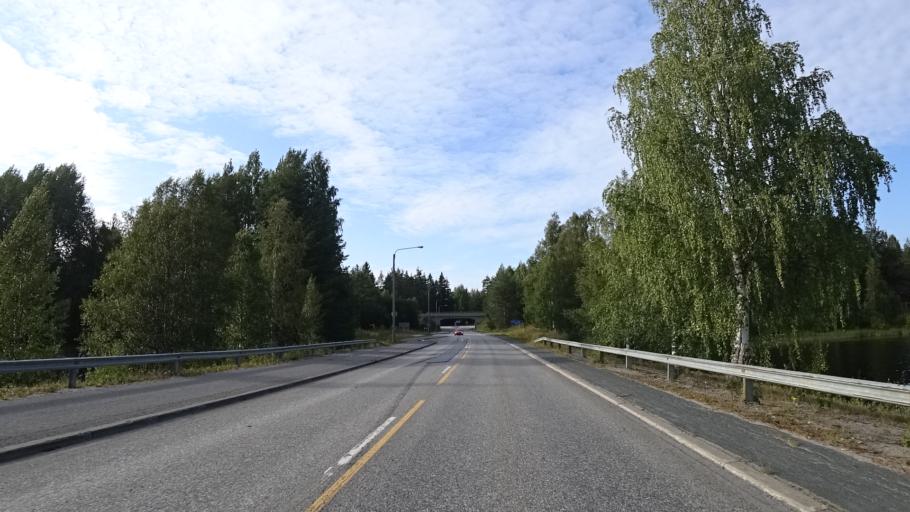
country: FI
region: North Karelia
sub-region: Joensuu
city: Eno
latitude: 62.8059
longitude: 30.1522
